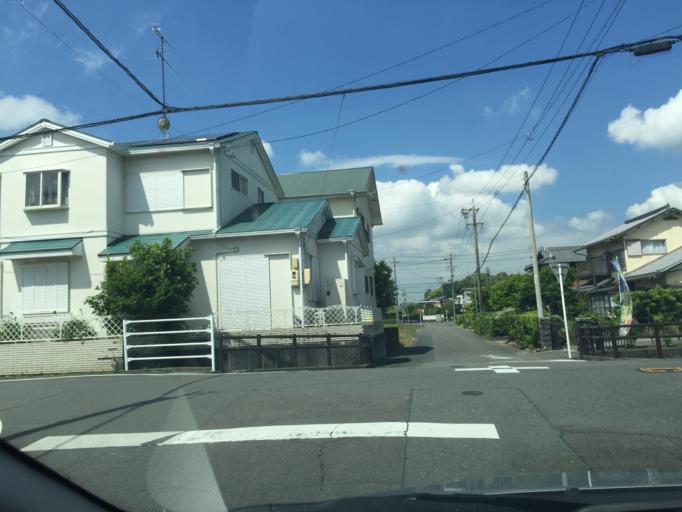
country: JP
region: Shizuoka
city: Kakegawa
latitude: 34.7830
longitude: 138.0144
